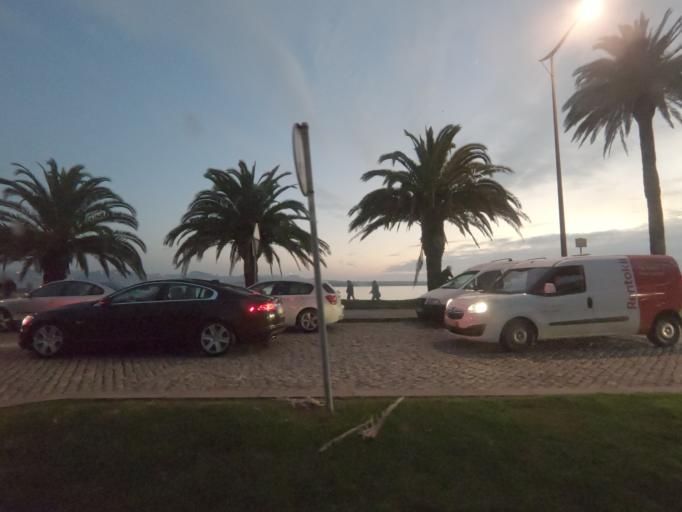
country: PT
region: Porto
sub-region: Vila Nova de Gaia
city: Canidelo
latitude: 41.1477
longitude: -8.6678
